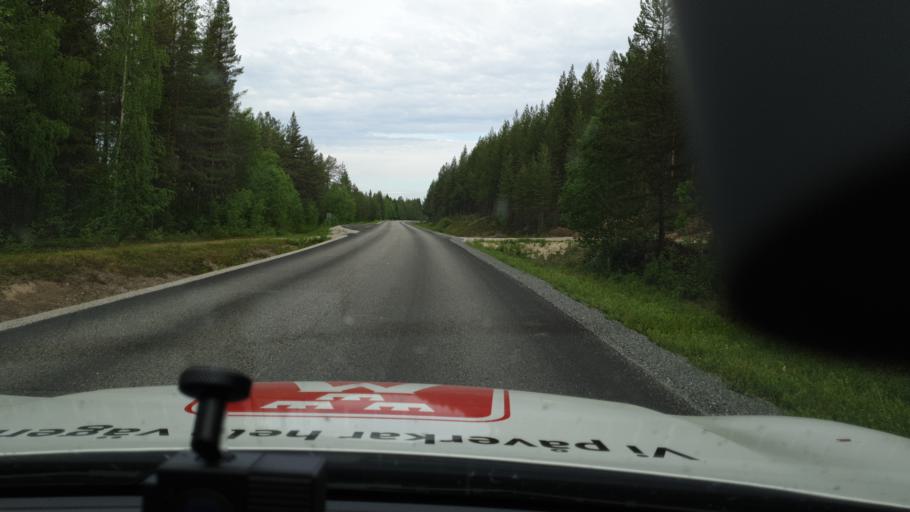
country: SE
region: Vaesterbotten
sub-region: Mala Kommun
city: Mala
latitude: 64.9132
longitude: 18.6549
